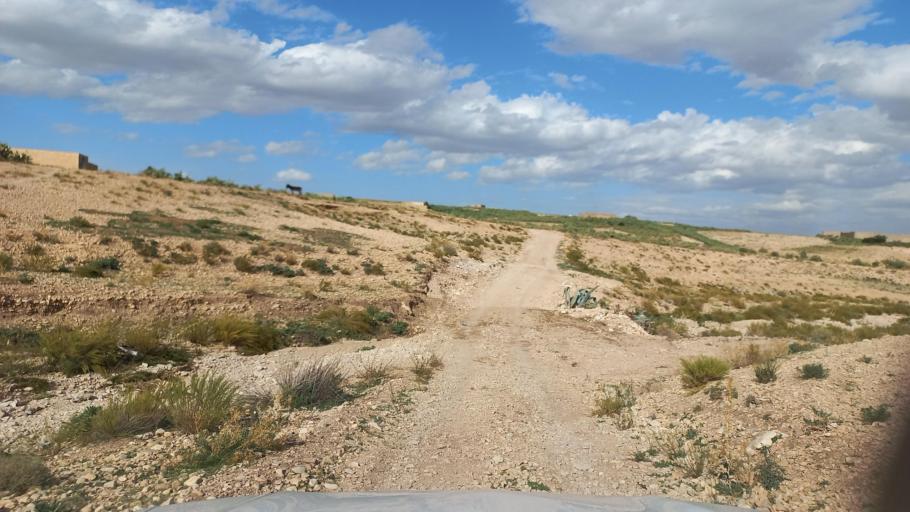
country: TN
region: Al Qasrayn
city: Sbiba
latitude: 35.4547
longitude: 9.0741
